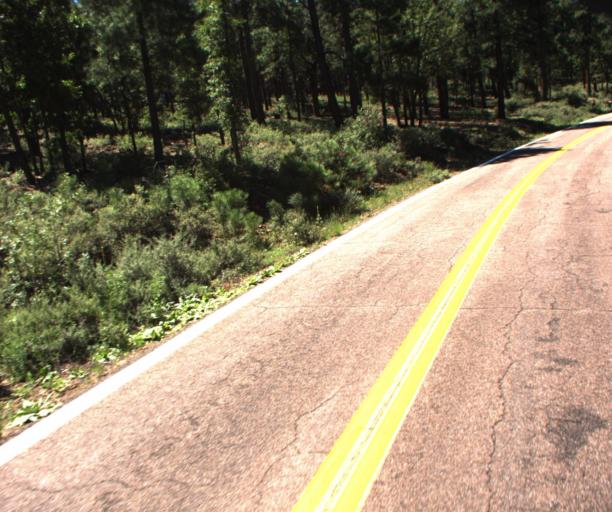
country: US
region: Arizona
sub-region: Greenlee County
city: Morenci
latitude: 33.4955
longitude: -109.3319
